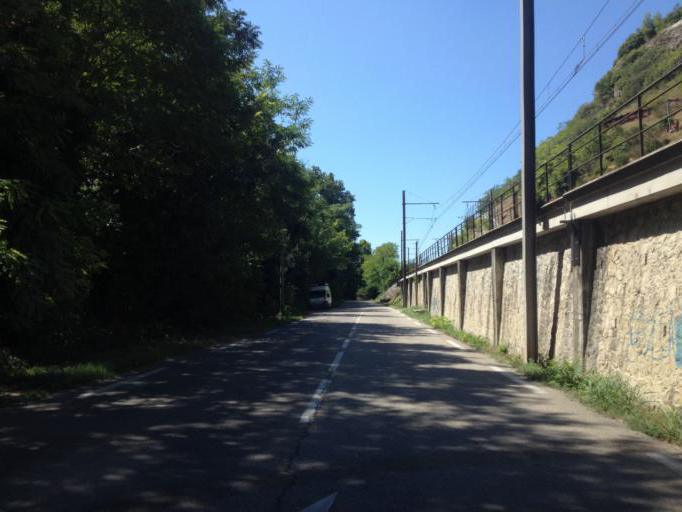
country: FR
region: Languedoc-Roussillon
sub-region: Departement du Gard
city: Villeneuve-les-Avignon
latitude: 43.9810
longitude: 4.8041
